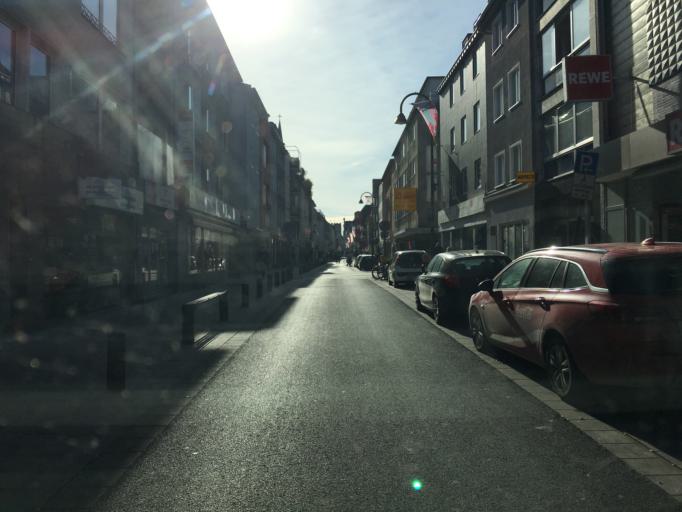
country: DE
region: North Rhine-Westphalia
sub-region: Regierungsbezirk Koln
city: Altstadt Sud
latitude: 50.9261
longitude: 6.9581
